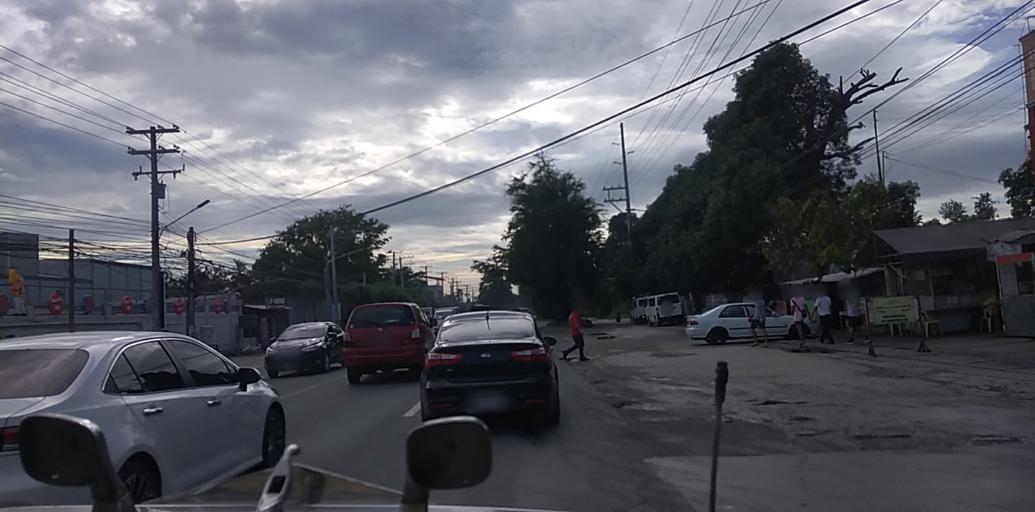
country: PH
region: Central Luzon
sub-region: Province of Pampanga
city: Telabastagan
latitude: 15.1007
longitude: 120.6206
